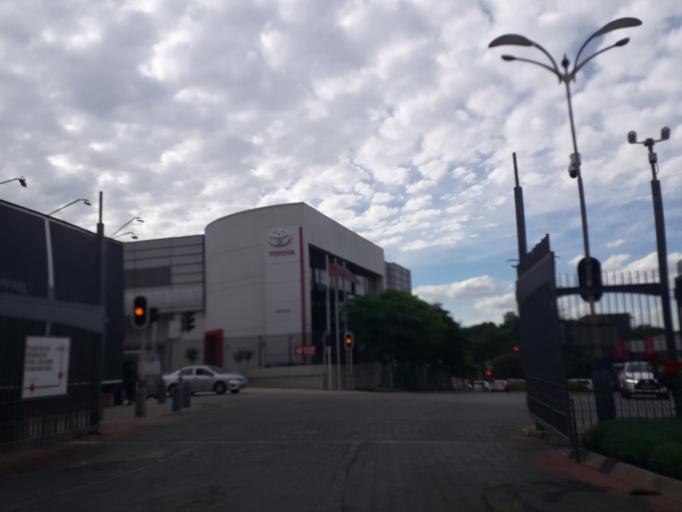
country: ZA
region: Gauteng
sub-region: City of Johannesburg Metropolitan Municipality
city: Johannesburg
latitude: -26.1306
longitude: 28.0690
